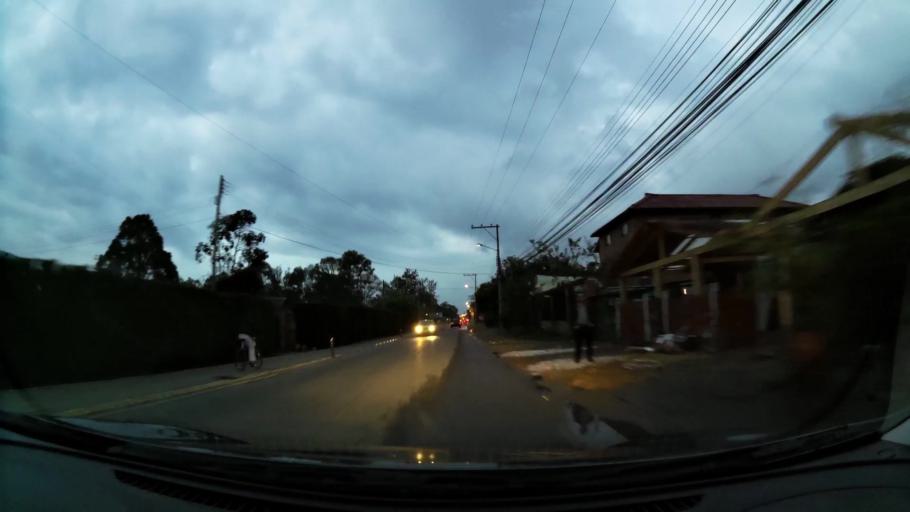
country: CO
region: Cundinamarca
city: Chia
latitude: 4.8465
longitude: -74.0654
